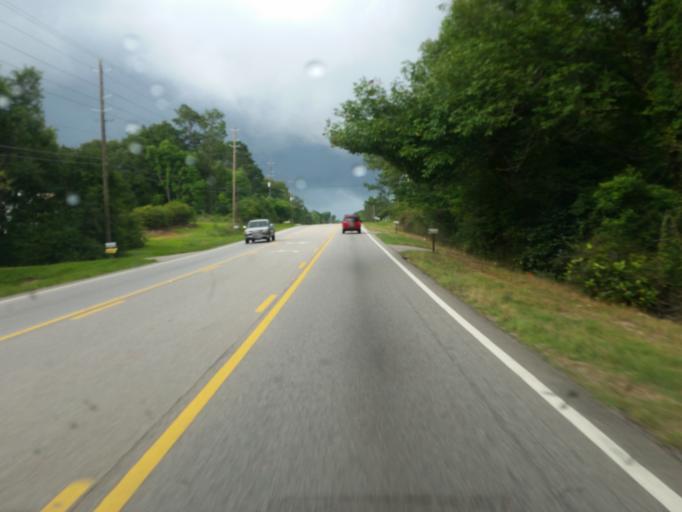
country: US
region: Mississippi
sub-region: Jackson County
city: Hurley
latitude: 30.7948
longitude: -88.3144
